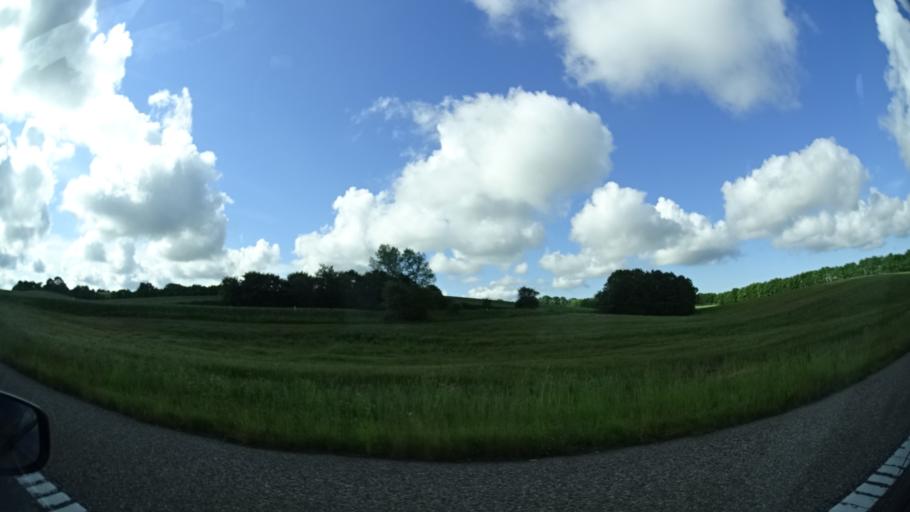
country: DK
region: Central Jutland
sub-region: Syddjurs Kommune
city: Ronde
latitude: 56.2959
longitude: 10.5641
